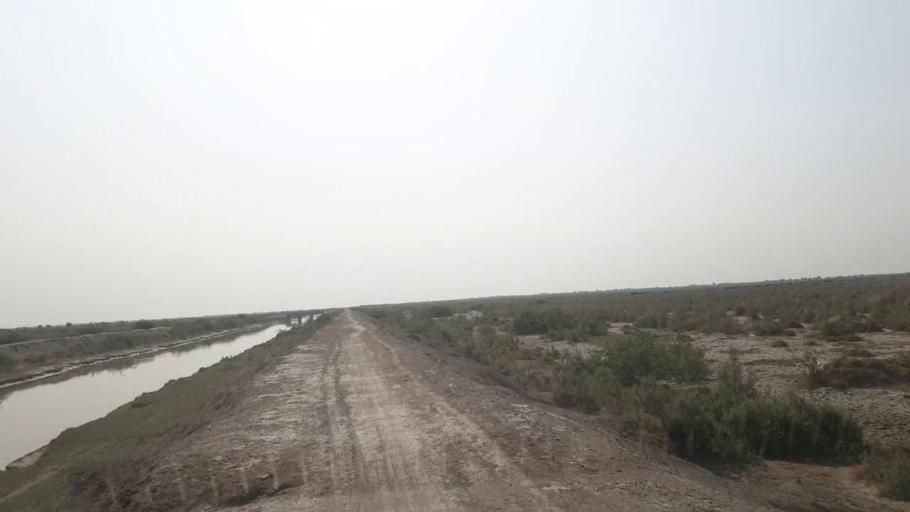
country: PK
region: Sindh
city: Kadhan
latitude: 24.3828
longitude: 68.8987
